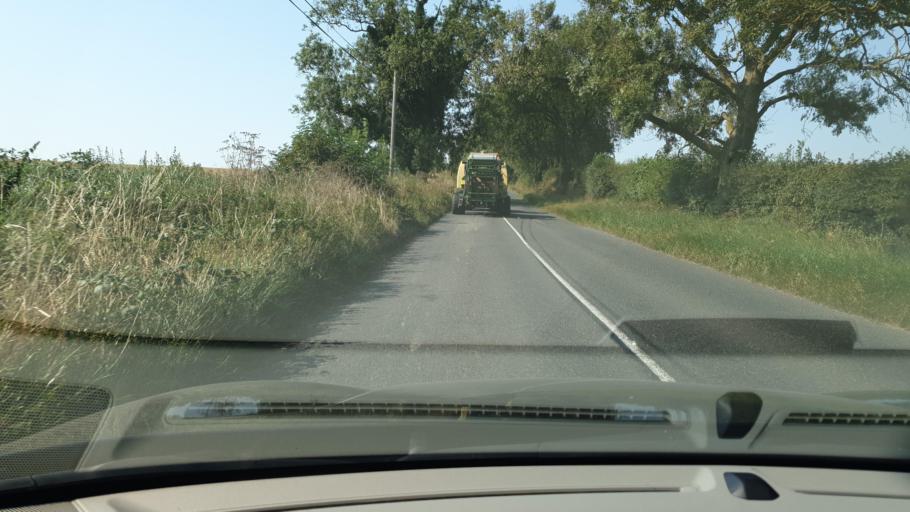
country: IE
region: Leinster
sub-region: An Mhi
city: Athboy
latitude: 53.5937
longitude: -6.8652
